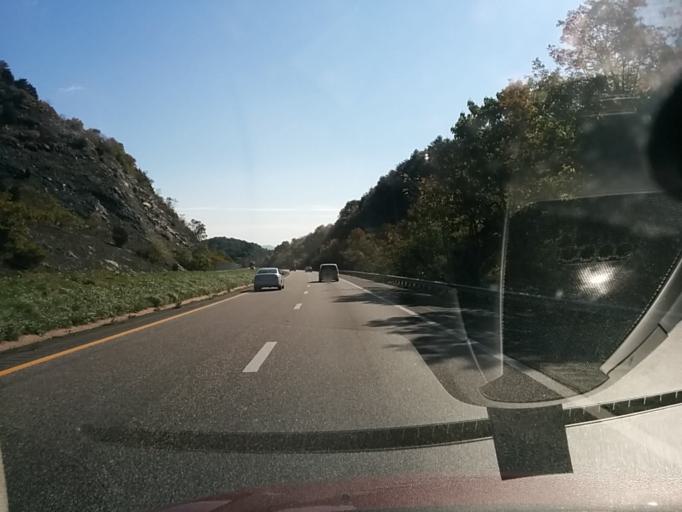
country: US
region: Virginia
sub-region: Augusta County
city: Dooms
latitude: 38.0437
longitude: -78.8122
